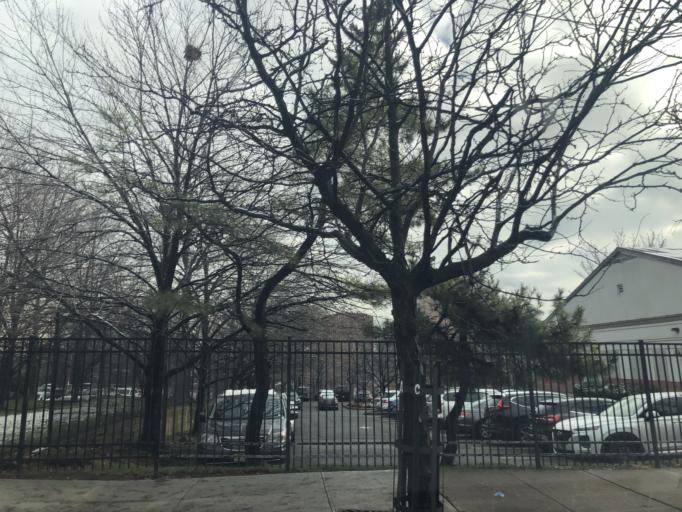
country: US
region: New Jersey
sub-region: Hudson County
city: Hoboken
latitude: 40.7366
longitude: -74.0490
